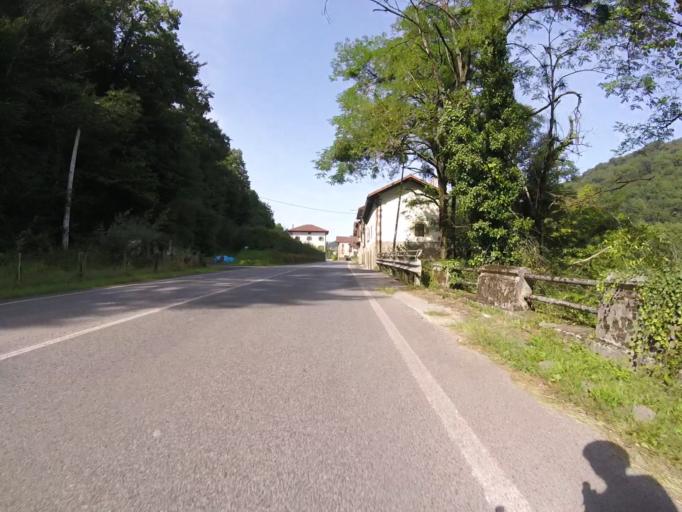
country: ES
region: Navarre
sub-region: Provincia de Navarra
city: Doneztebe
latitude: 43.1372
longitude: -1.6135
